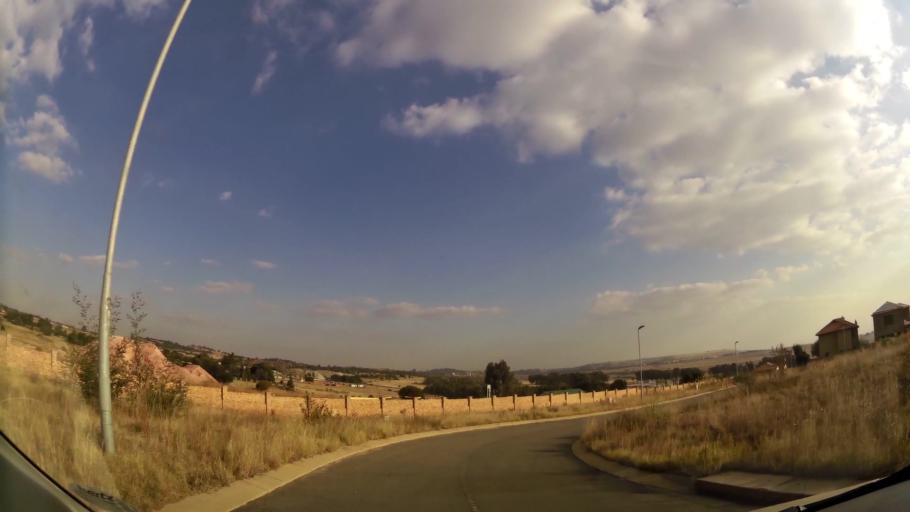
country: ZA
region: Gauteng
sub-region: West Rand District Municipality
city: Krugersdorp
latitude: -26.1036
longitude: 27.7324
